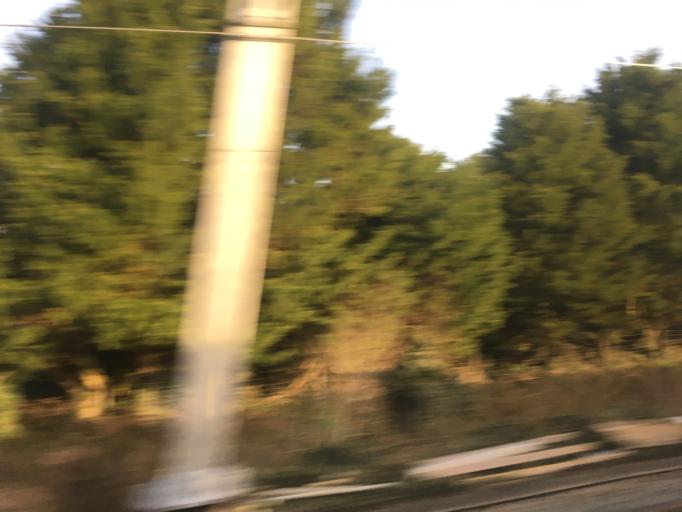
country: GB
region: England
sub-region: Wiltshire
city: Norton
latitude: 51.5451
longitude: -2.1535
